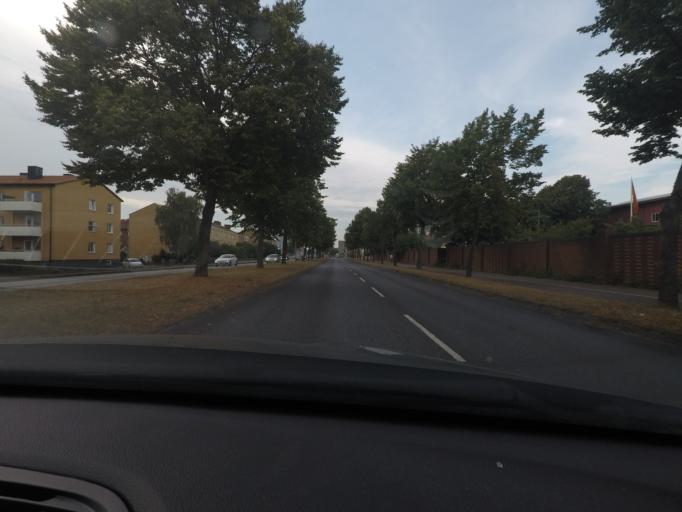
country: SE
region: Halland
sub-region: Halmstads Kommun
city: Halmstad
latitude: 56.6668
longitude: 12.8771
